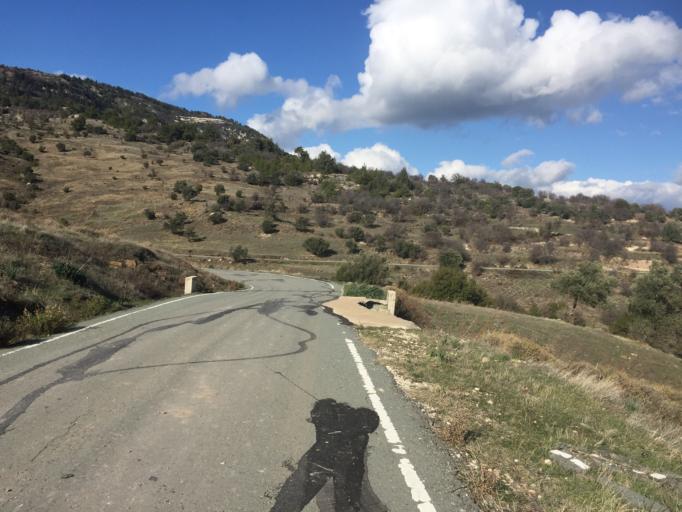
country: CY
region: Limassol
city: Pachna
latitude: 34.8883
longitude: 32.6529
